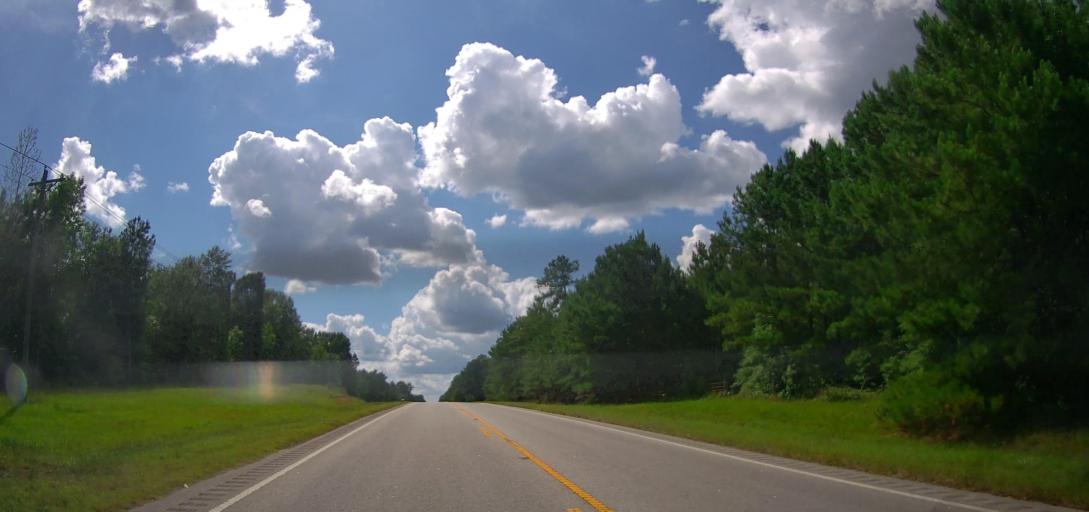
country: US
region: Alabama
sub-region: Macon County
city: Tuskegee
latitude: 32.4549
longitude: -85.5385
